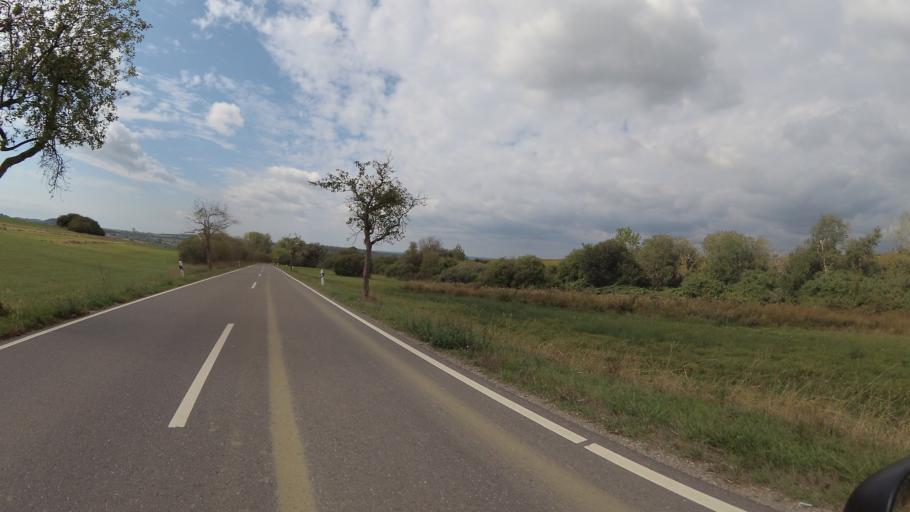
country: FR
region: Lorraine
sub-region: Departement de la Moselle
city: Bliesbruck
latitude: 49.1327
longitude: 7.1618
